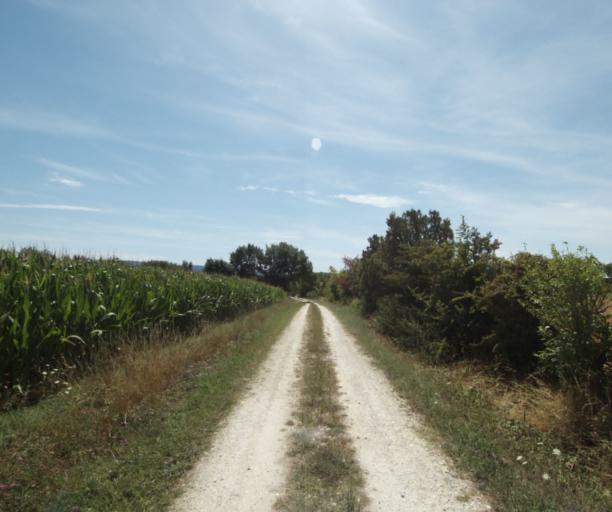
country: FR
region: Midi-Pyrenees
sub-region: Departement de la Haute-Garonne
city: Revel
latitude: 43.5020
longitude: 2.0158
